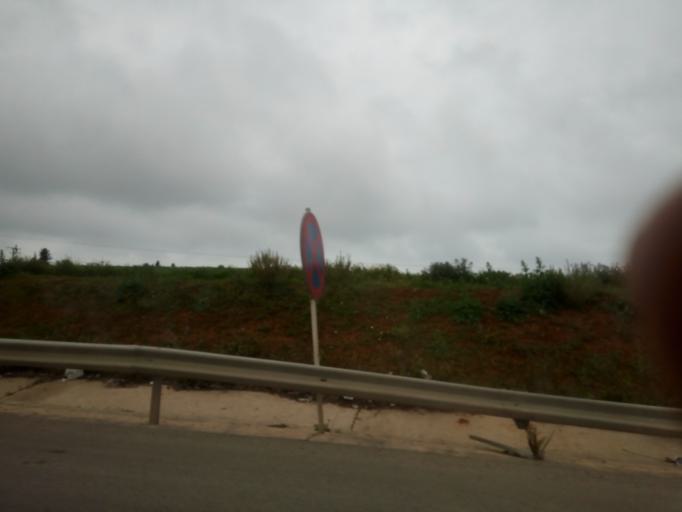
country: DZ
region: Tipaza
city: Bou Ismail
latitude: 36.5932
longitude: 2.6276
